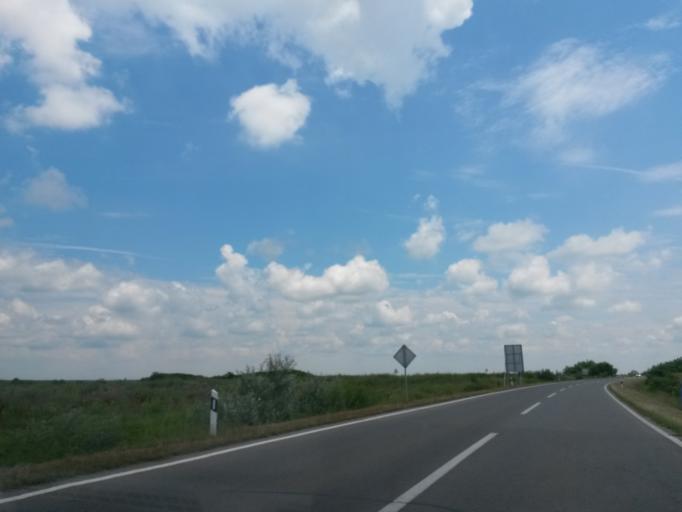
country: HR
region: Osjecko-Baranjska
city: Tenja
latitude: 45.5251
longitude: 18.7837
